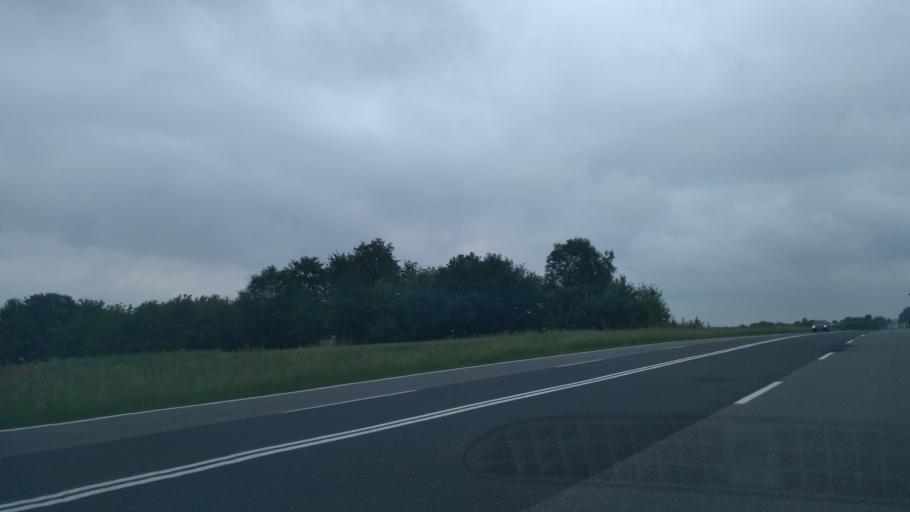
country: PL
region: Subcarpathian Voivodeship
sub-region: Powiat przeworski
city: Nowosielce
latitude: 50.0661
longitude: 22.4010
